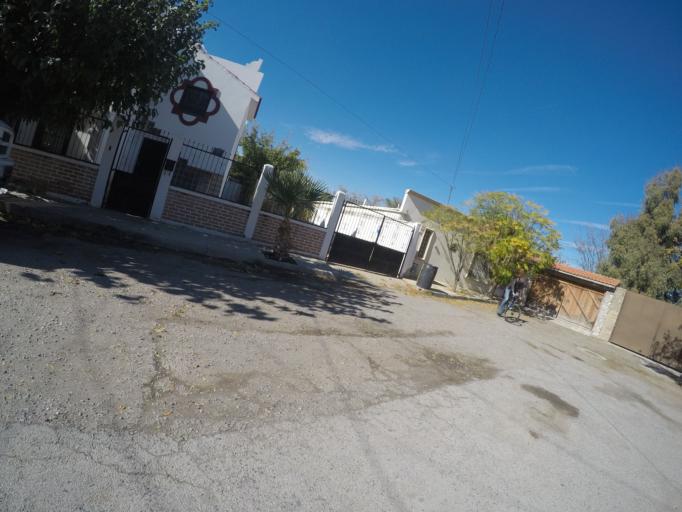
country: MX
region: Chihuahua
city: Ciudad Juarez
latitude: 31.7298
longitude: -106.4297
